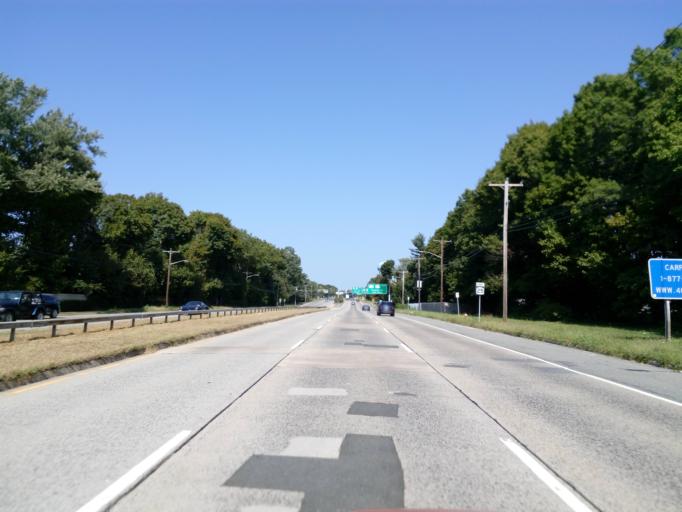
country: US
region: New York
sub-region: Nassau County
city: Jericho
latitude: 40.7891
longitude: -73.5445
